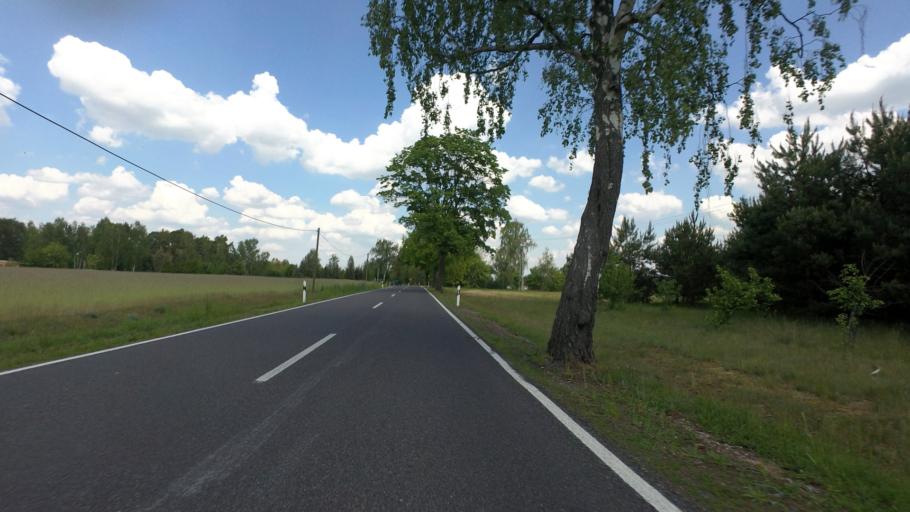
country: DE
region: Brandenburg
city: Lieberose
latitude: 51.9797
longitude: 14.2182
